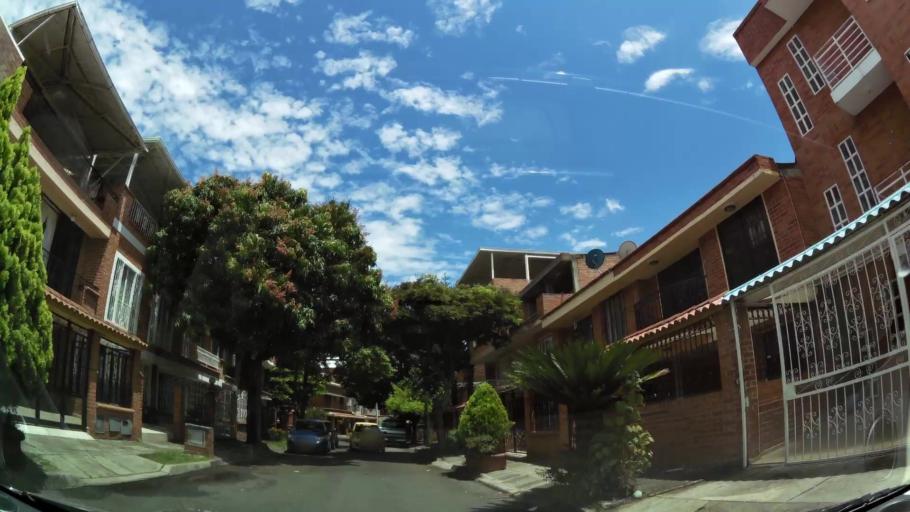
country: CO
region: Valle del Cauca
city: Cali
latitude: 3.3881
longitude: -76.5148
